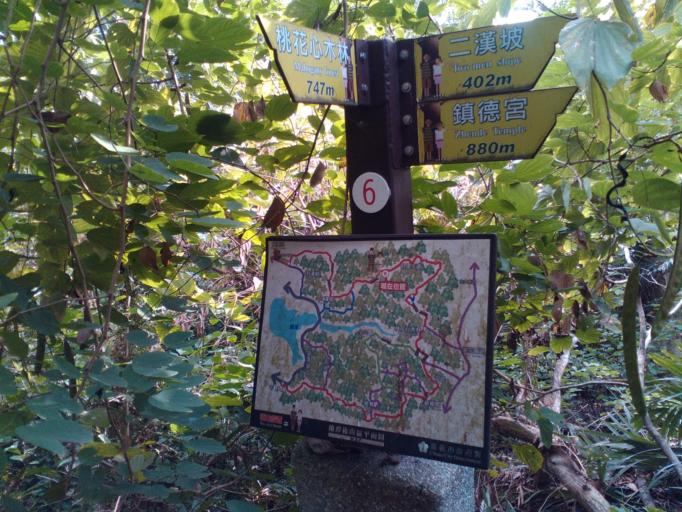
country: TW
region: Taiwan
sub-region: Chiayi
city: Jiayi Shi
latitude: 23.4791
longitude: 120.4935
